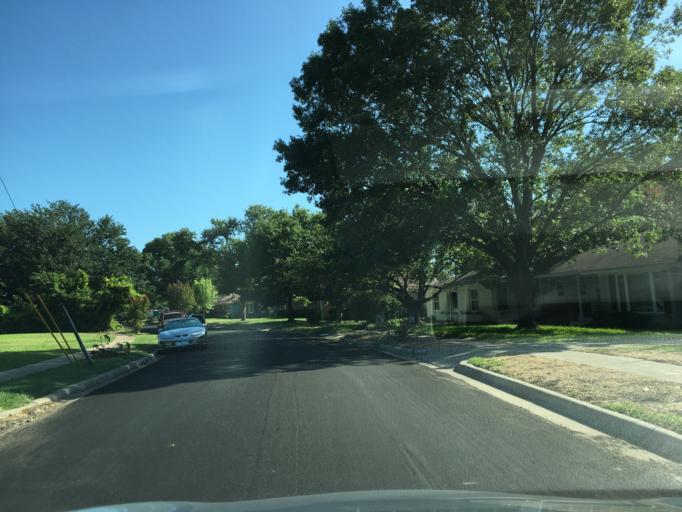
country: US
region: Texas
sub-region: Dallas County
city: Garland
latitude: 32.8593
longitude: -96.7069
